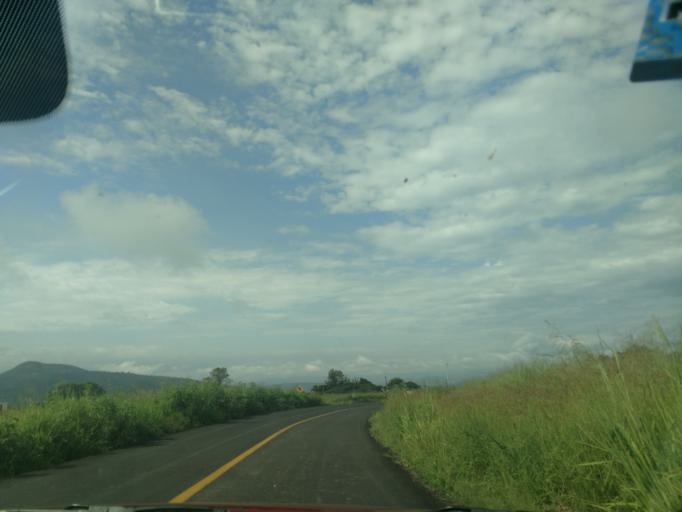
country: MX
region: Jalisco
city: El Salto
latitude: 20.4338
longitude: -104.4505
